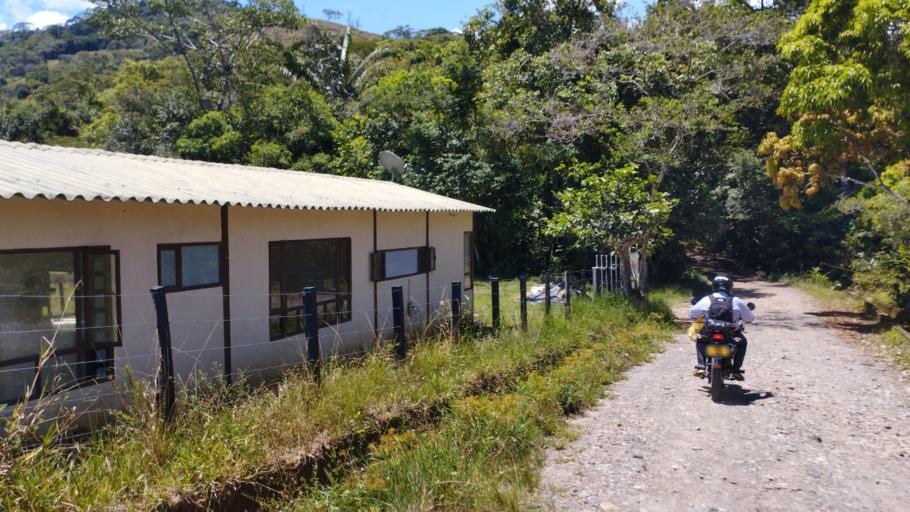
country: CO
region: Boyaca
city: San Luis de Gaceno
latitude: 4.7945
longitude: -73.1193
